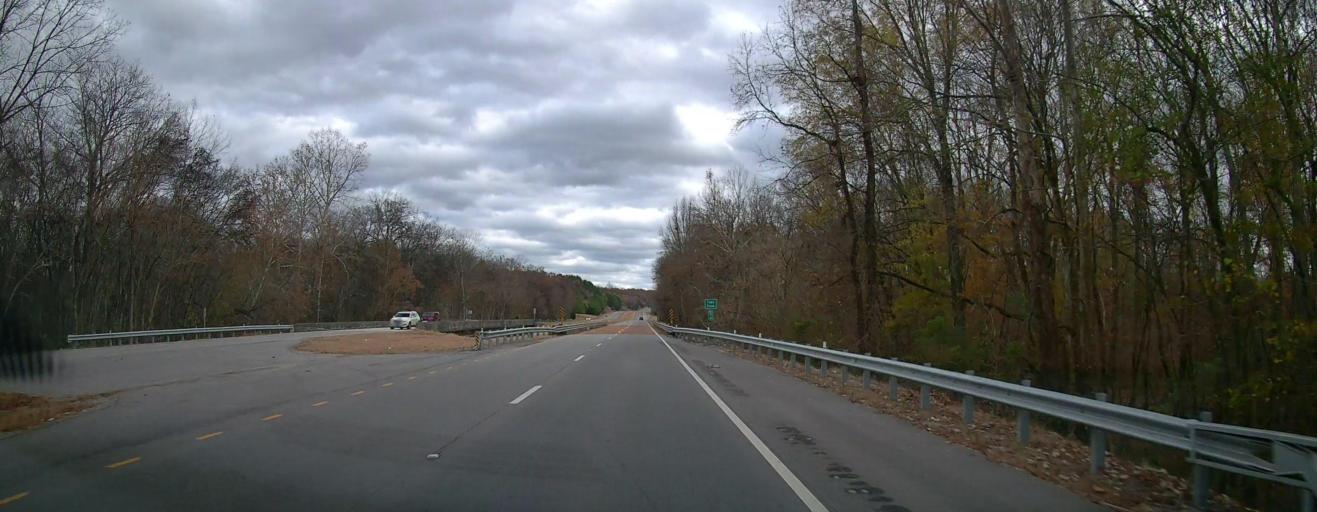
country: US
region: Alabama
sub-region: Lawrence County
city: Town Creek
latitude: 34.6319
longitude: -87.4881
